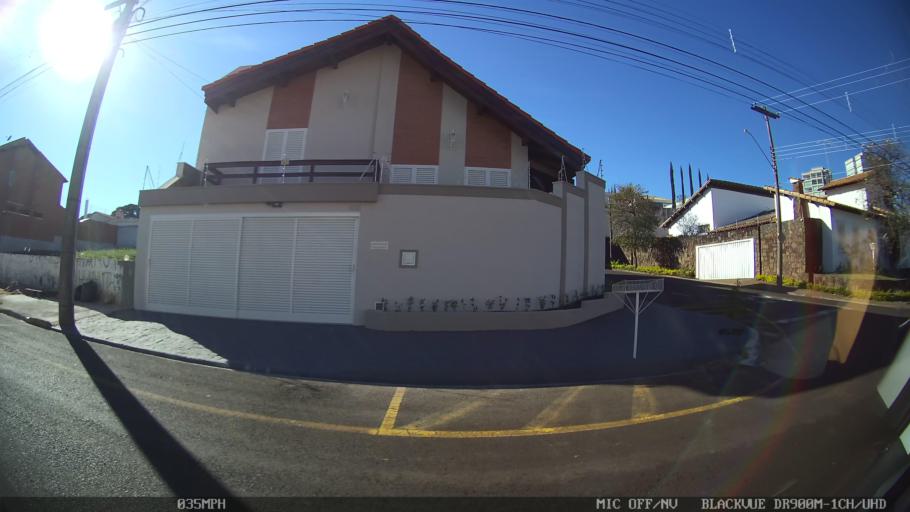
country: BR
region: Sao Paulo
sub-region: Franca
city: Franca
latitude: -20.5455
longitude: -47.4058
